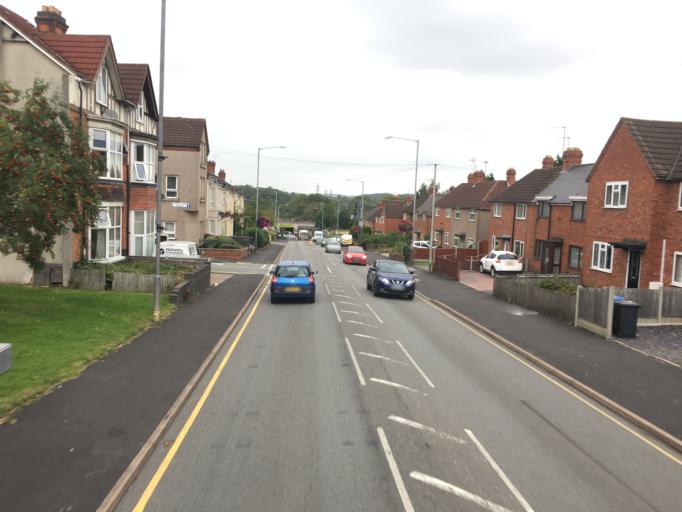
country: GB
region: England
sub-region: Warwickshire
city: Rugby
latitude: 52.3787
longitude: -1.2648
